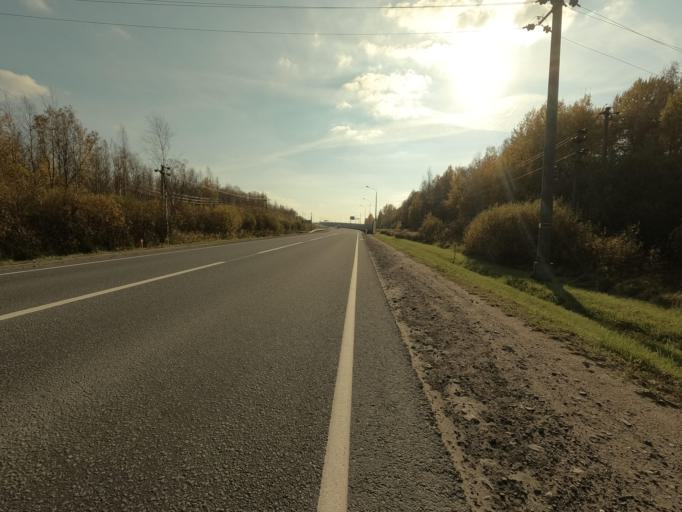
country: RU
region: Leningrad
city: Mga
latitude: 59.7634
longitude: 31.0947
